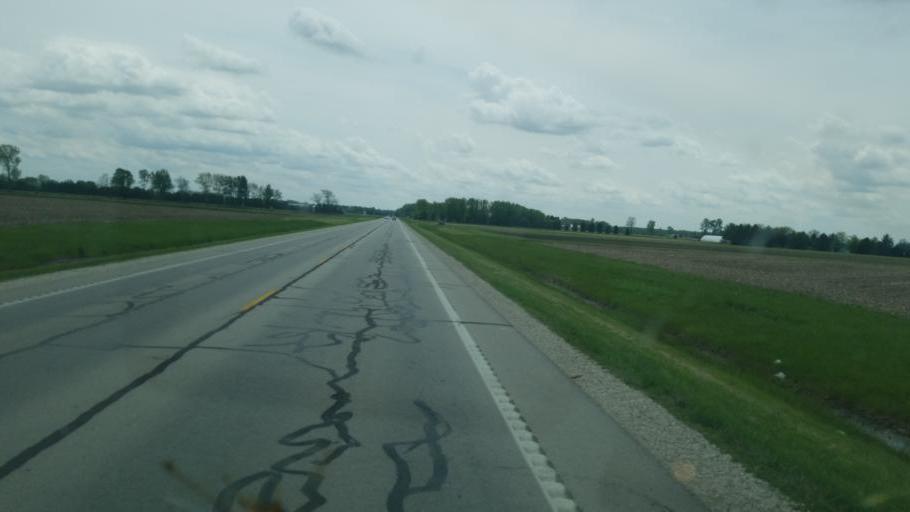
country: US
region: Ohio
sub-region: Sandusky County
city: Stony Prairie
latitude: 41.3156
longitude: -83.1684
